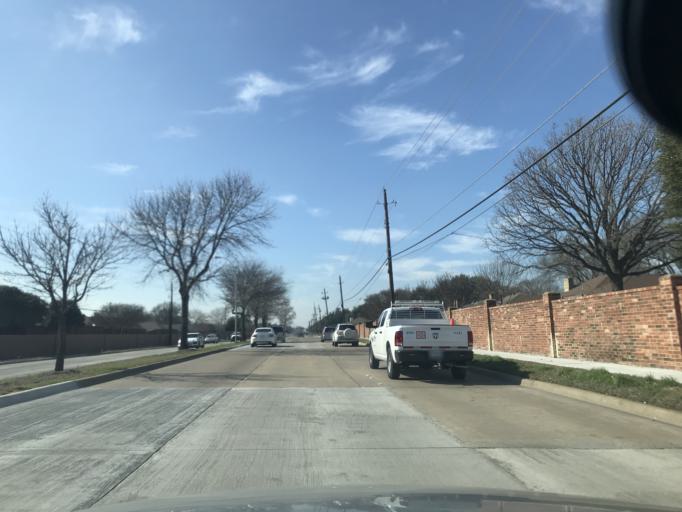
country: US
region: Texas
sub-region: Collin County
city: Plano
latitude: 33.0411
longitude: -96.7270
